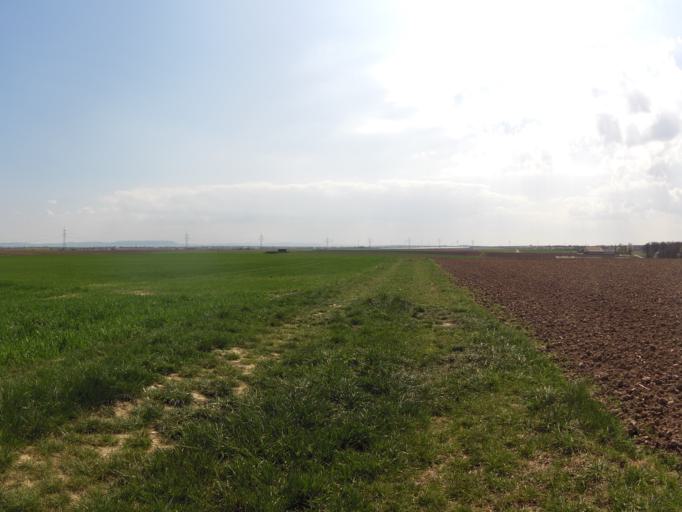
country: DE
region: Bavaria
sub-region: Regierungsbezirk Unterfranken
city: Oberpleichfeld
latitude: 49.8503
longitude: 10.0753
